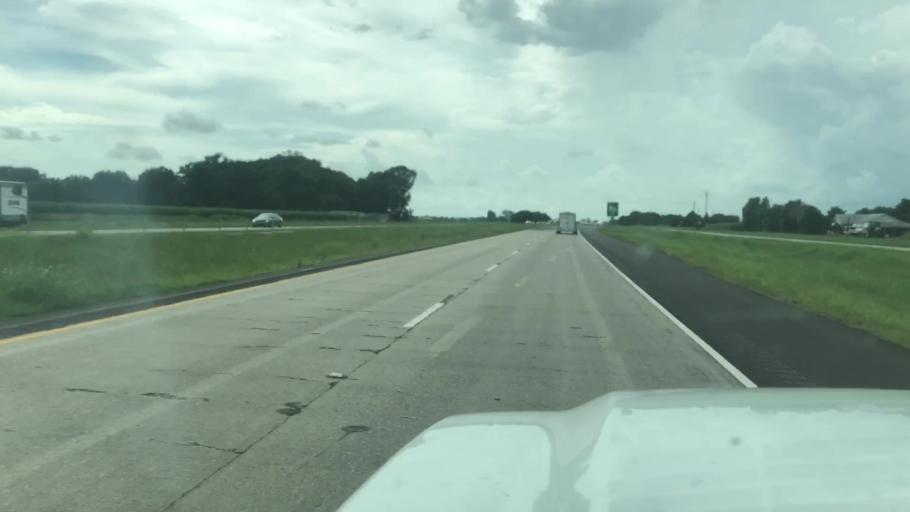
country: US
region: Louisiana
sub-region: Iberia Parish
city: Jeanerette
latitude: 29.8621
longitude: -91.6241
